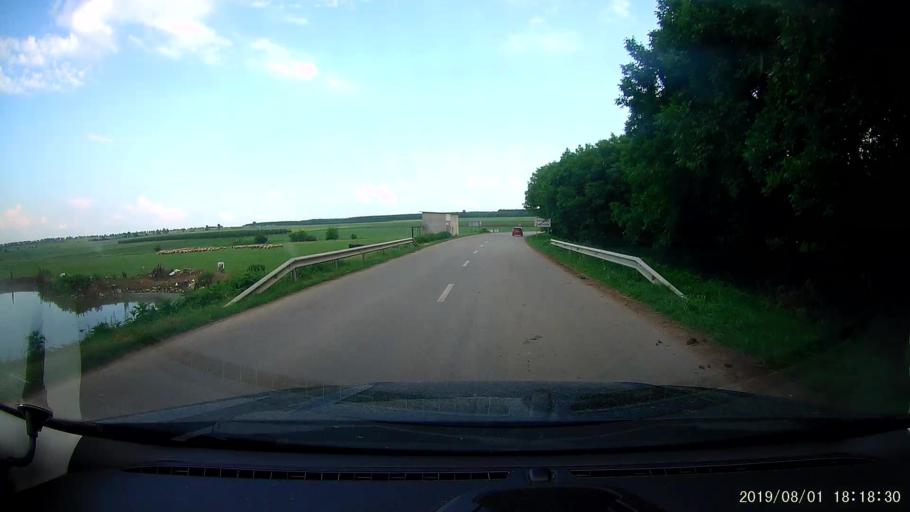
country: BG
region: Shumen
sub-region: Obshtina Kaolinovo
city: Kaolinovo
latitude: 43.6975
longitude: 27.0820
